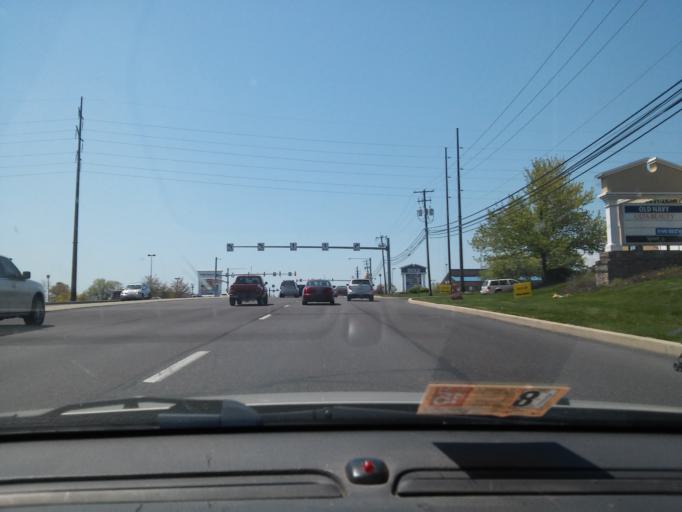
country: US
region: Pennsylvania
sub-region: Dauphin County
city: Paxtonia
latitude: 40.3127
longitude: -76.8003
